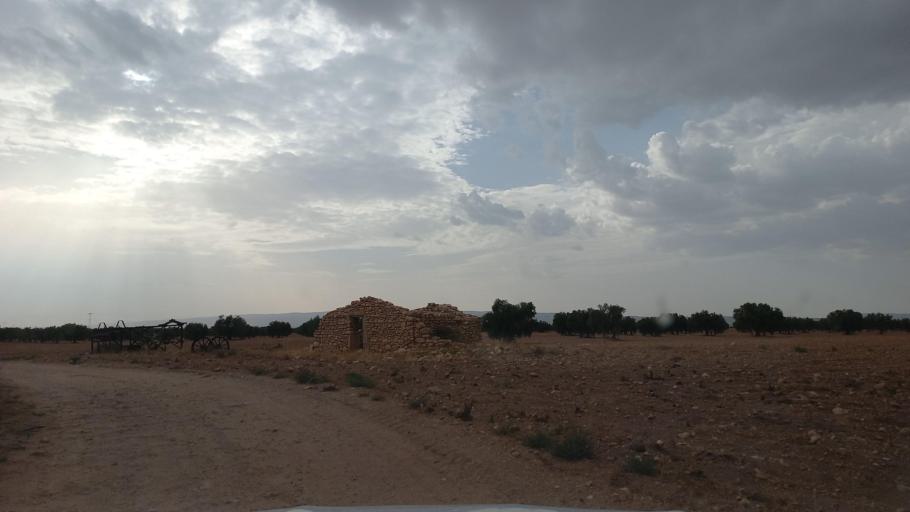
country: TN
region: Al Qasrayn
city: Sbiba
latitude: 35.2963
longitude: 9.0760
